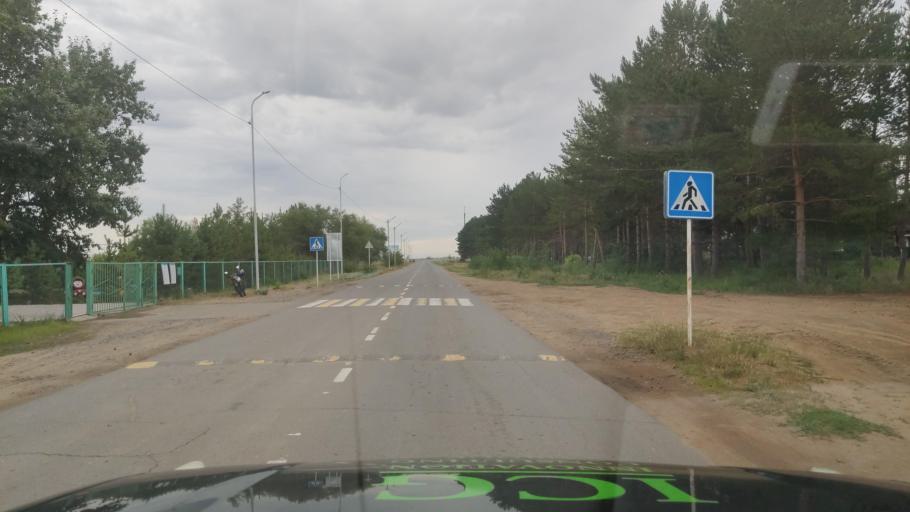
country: KZ
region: Pavlodar
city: Leninskiy
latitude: 52.5395
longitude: 76.8080
